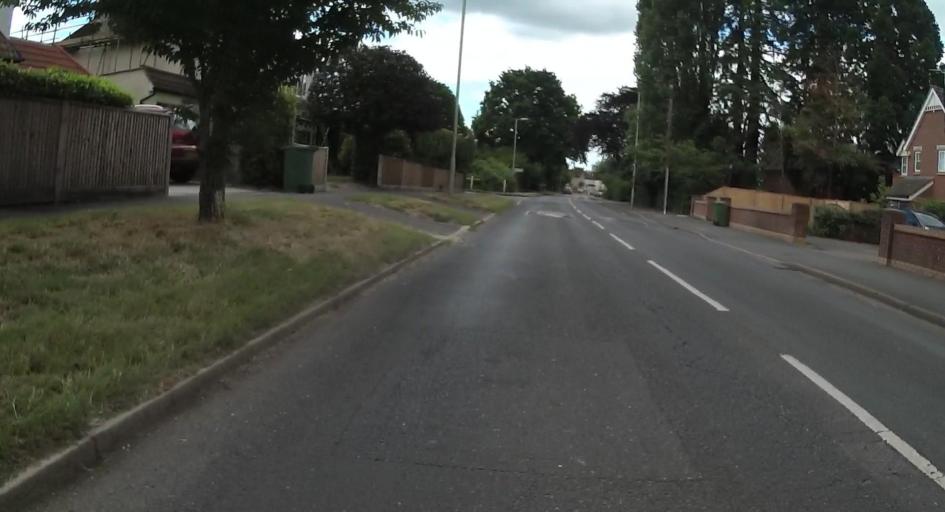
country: GB
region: England
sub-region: Hampshire
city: Aldershot
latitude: 51.2373
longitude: -0.7645
